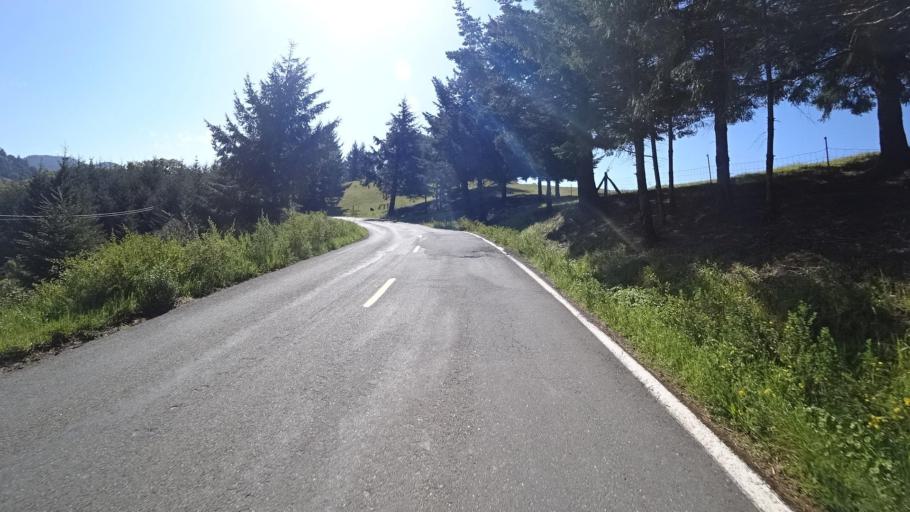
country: US
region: California
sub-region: Humboldt County
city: Redway
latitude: 40.1084
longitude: -123.7508
